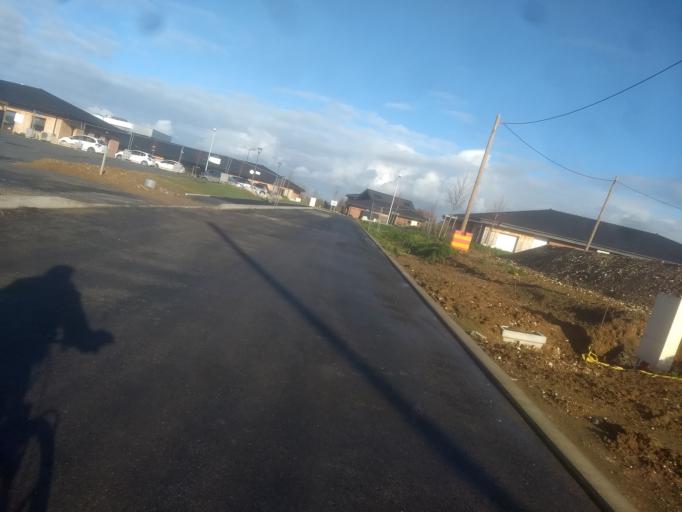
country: FR
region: Nord-Pas-de-Calais
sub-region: Departement du Pas-de-Calais
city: Anzin-Saint-Aubin
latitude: 50.3047
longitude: 2.7311
